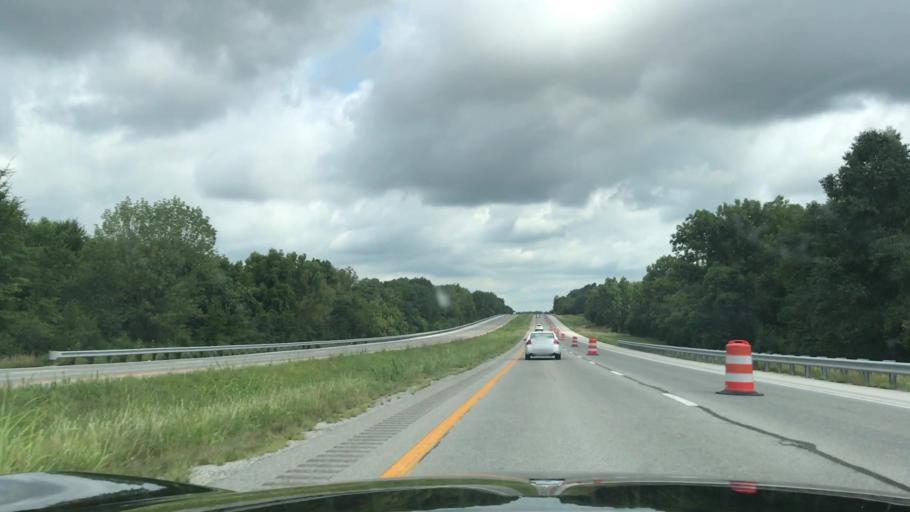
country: US
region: Kentucky
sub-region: Butler County
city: Morgantown
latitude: 37.1059
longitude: -86.6402
